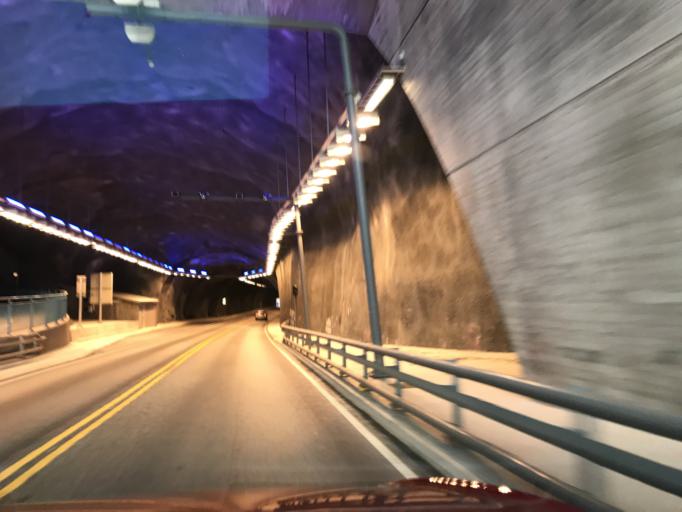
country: NO
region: Hordaland
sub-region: Ulvik
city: Ulvik
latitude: 60.4730
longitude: 6.8370
